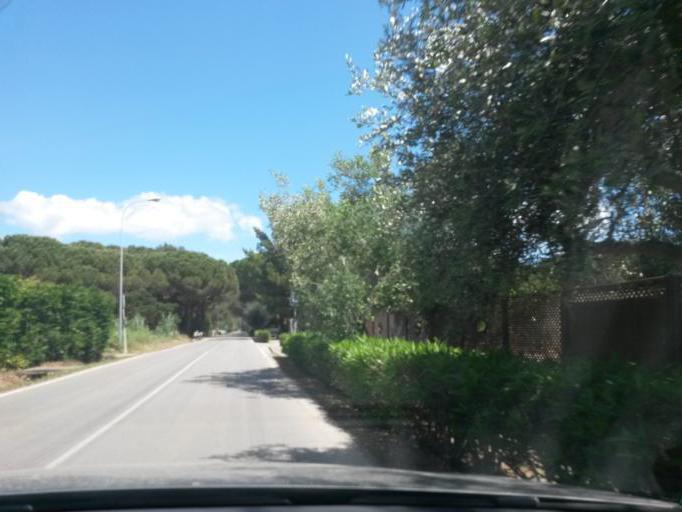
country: IT
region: Tuscany
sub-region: Provincia di Livorno
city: Portoferraio
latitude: 42.7618
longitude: 10.3026
